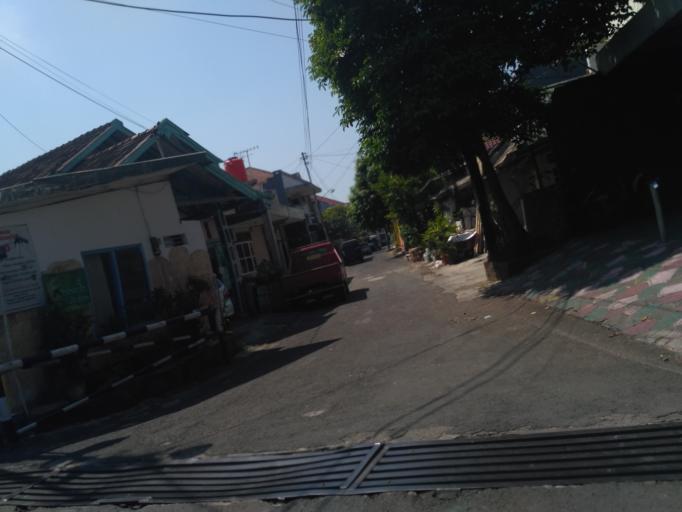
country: ID
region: Central Java
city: Semarang
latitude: -7.0001
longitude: 110.4256
